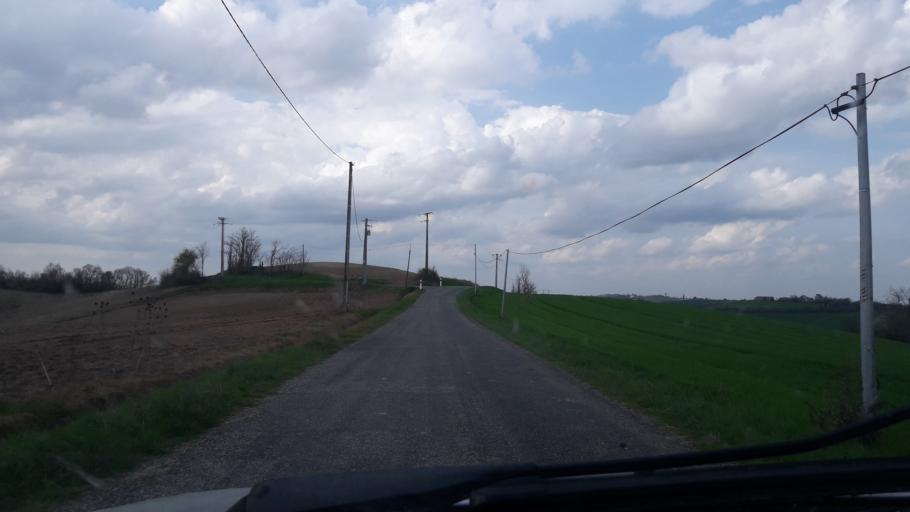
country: FR
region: Midi-Pyrenees
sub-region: Departement de la Haute-Garonne
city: Montesquieu-Volvestre
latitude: 43.2021
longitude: 1.3097
